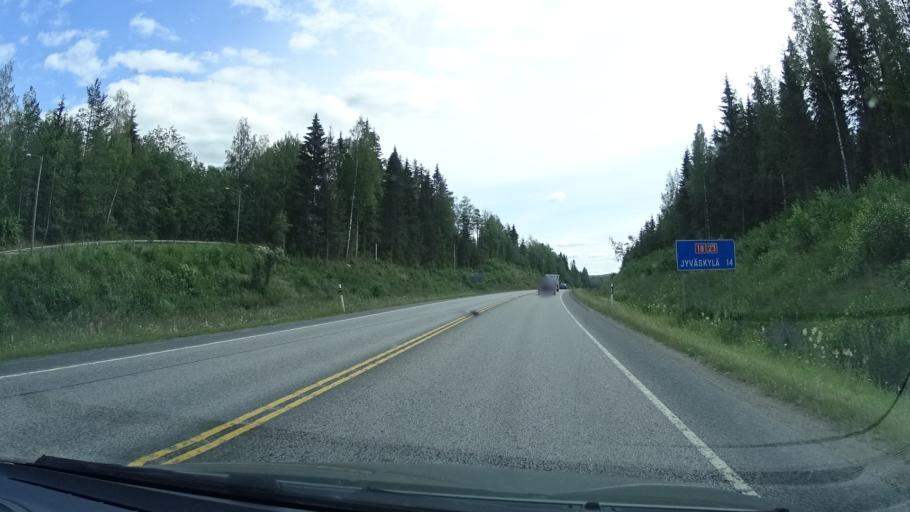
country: FI
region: Central Finland
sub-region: Jyvaeskylae
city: Jyvaeskylae
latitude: 62.2644
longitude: 25.5827
